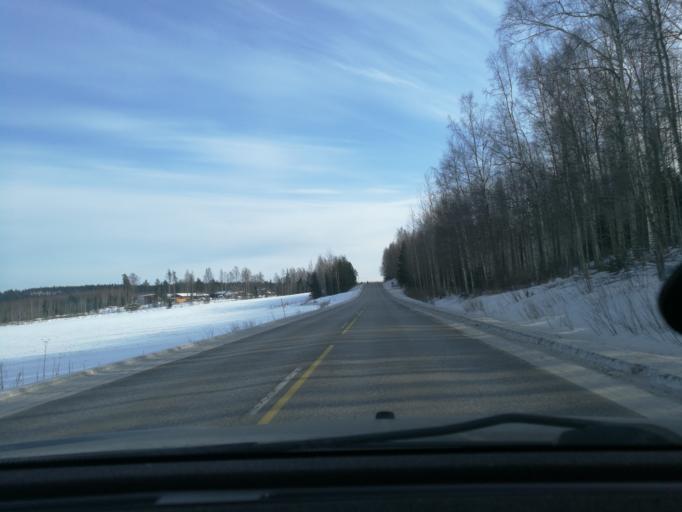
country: FI
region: Uusimaa
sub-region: Helsinki
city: Saukkola
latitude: 60.4244
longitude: 24.0363
